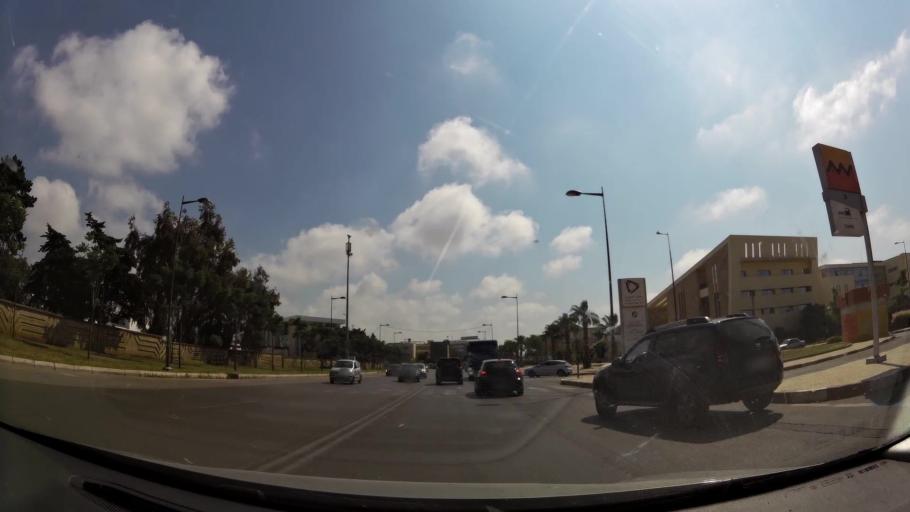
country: MA
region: Rabat-Sale-Zemmour-Zaer
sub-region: Rabat
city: Rabat
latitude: 33.9757
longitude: -6.8698
